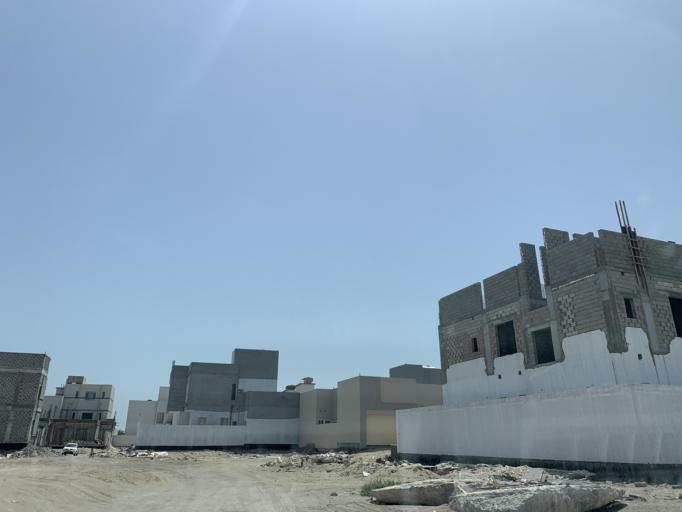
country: BH
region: Northern
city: Sitrah
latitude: 26.1486
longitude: 50.5994
